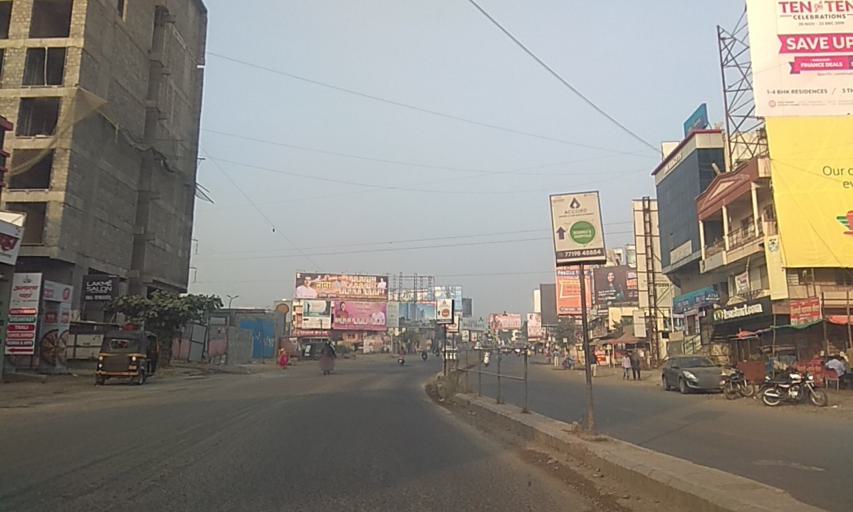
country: IN
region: Maharashtra
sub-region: Pune Division
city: Pimpri
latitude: 18.5909
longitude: 73.7418
